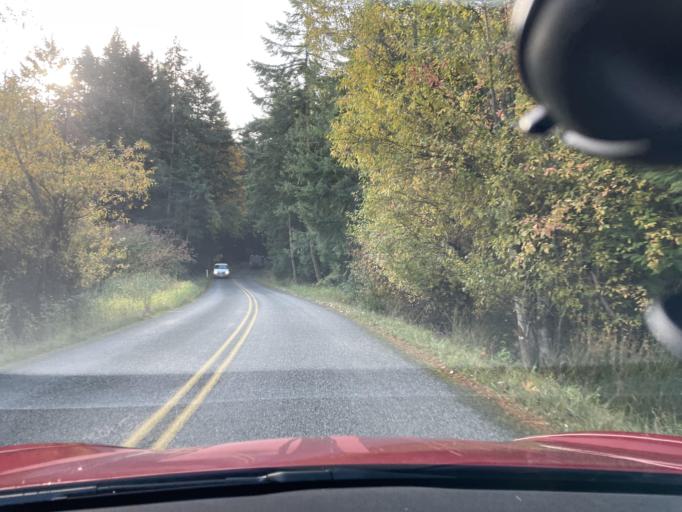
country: US
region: Washington
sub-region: San Juan County
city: Friday Harbor
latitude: 48.5229
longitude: -123.1455
